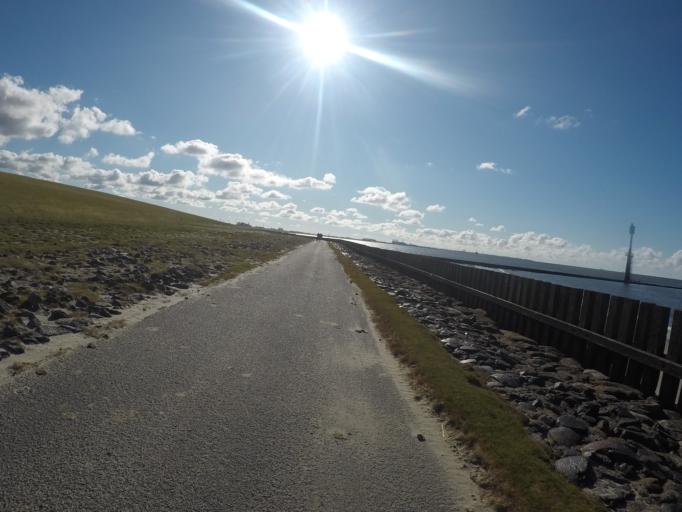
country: DE
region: Lower Saxony
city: Nordleda
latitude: 53.8330
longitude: 8.8363
